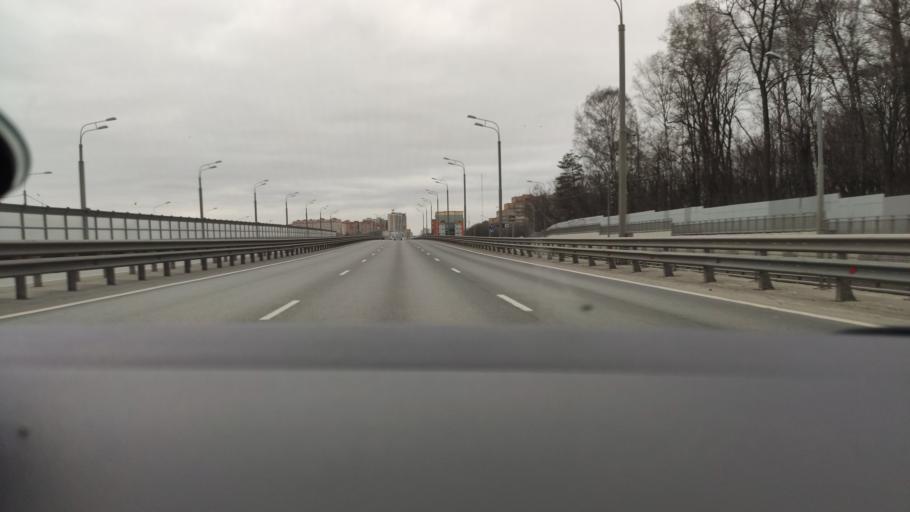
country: RU
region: Moskovskaya
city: Balashikha
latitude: 55.7964
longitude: 37.9601
